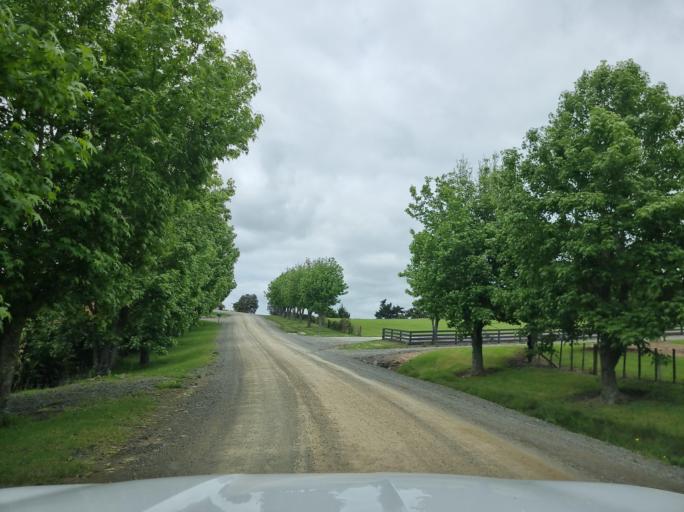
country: NZ
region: Auckland
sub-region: Auckland
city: Wellsford
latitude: -36.0922
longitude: 174.5294
